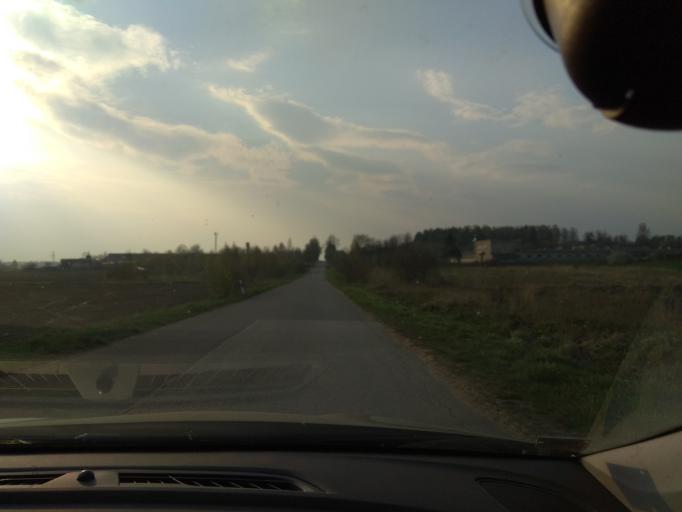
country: LT
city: Baltoji Voke
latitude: 54.5955
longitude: 25.1501
